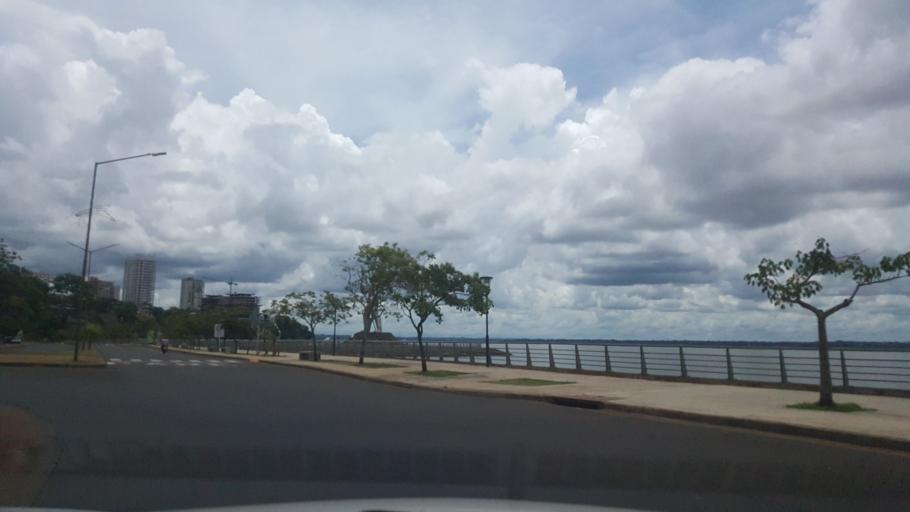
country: AR
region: Misiones
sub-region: Departamento de Capital
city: Posadas
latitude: -27.3616
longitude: -55.8867
